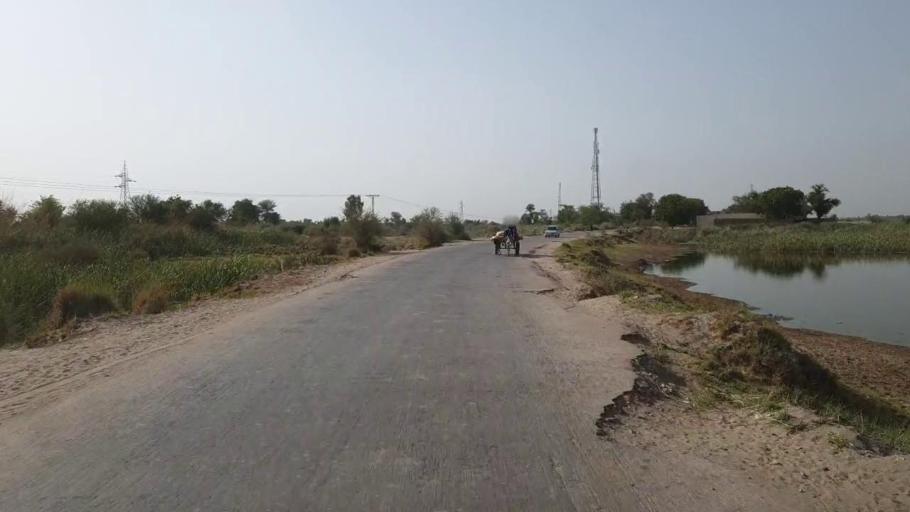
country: PK
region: Sindh
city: Sanghar
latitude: 26.2645
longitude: 68.9296
